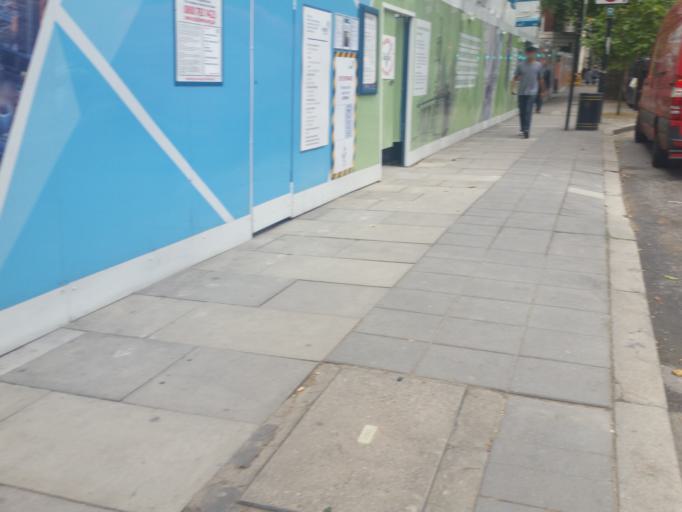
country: GB
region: England
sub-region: Greater London
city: Camden Town
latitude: 51.5218
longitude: -0.1599
